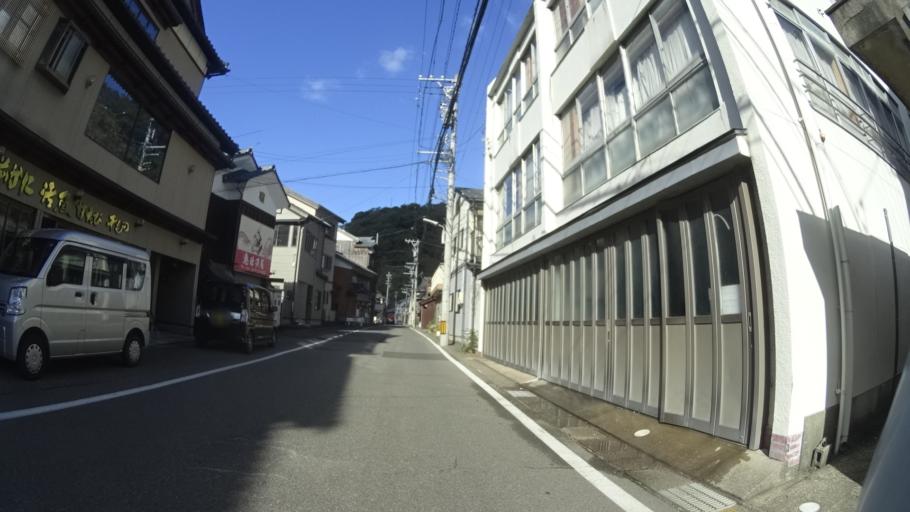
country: JP
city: Asahi
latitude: 35.9418
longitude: 135.9915
